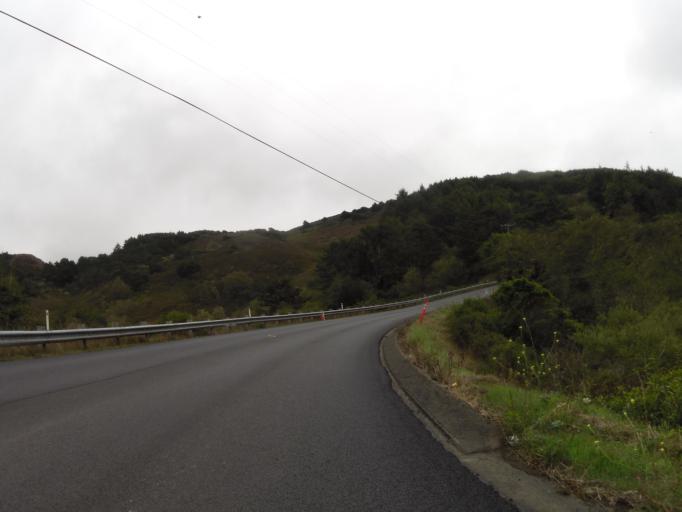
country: US
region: California
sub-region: Sonoma County
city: Monte Rio
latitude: 38.4324
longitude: -123.1006
